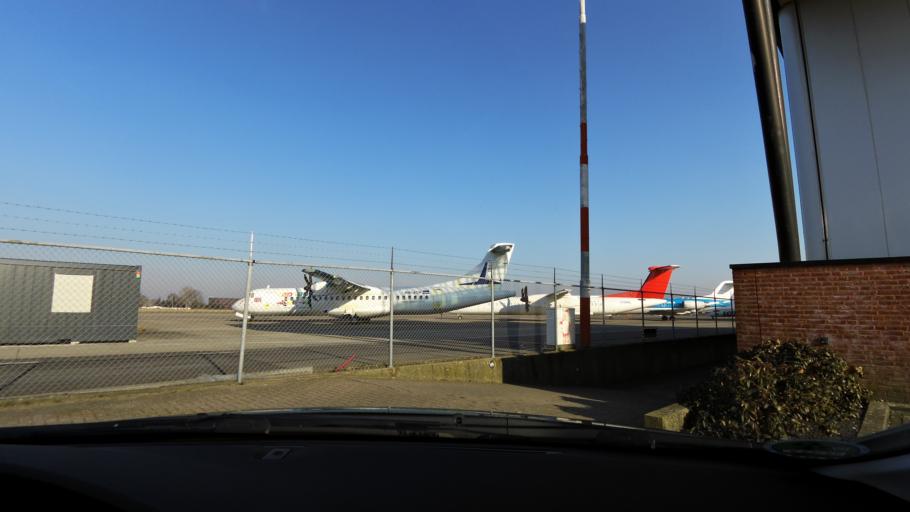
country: NL
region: Limburg
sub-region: Gemeente Beek
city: Beek
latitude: 50.9161
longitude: 5.7792
